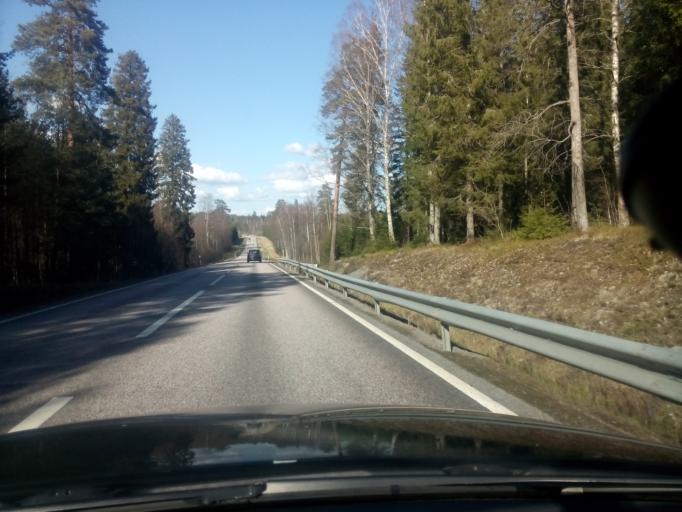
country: SE
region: Soedermanland
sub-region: Strangnas Kommun
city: Akers Styckebruk
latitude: 59.2311
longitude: 16.9303
